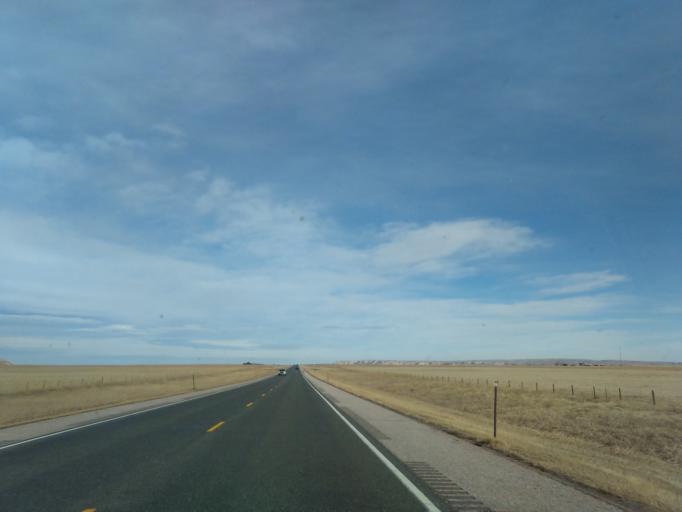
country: US
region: Wyoming
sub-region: Laramie County
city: Pine Bluffs
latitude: 41.6011
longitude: -104.2614
